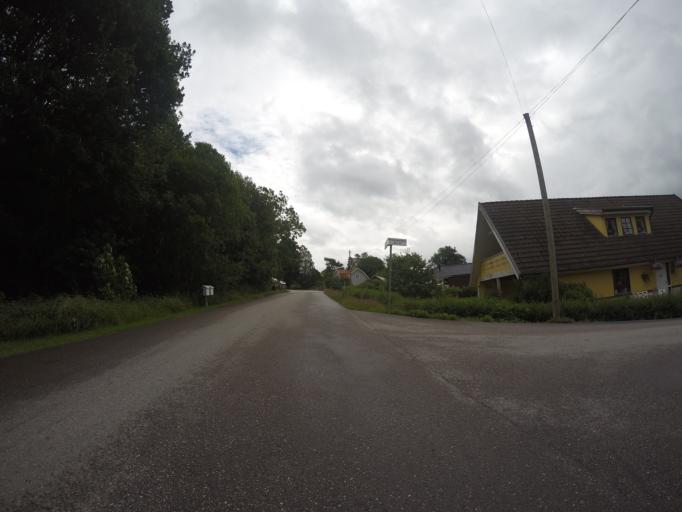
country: SE
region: Vaestra Goetaland
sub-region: Trollhattan
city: Sjuntorp
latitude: 58.2001
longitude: 12.2319
